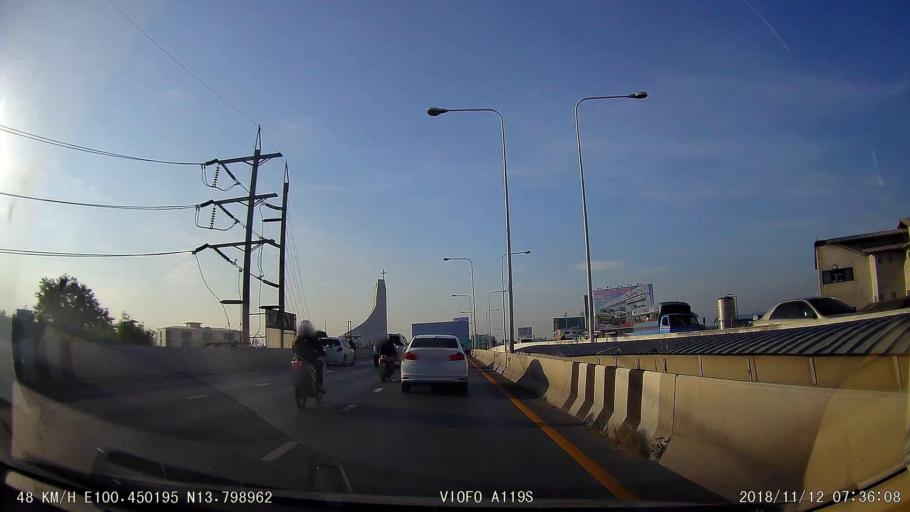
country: TH
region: Bangkok
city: Taling Chan
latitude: 13.7989
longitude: 100.4503
